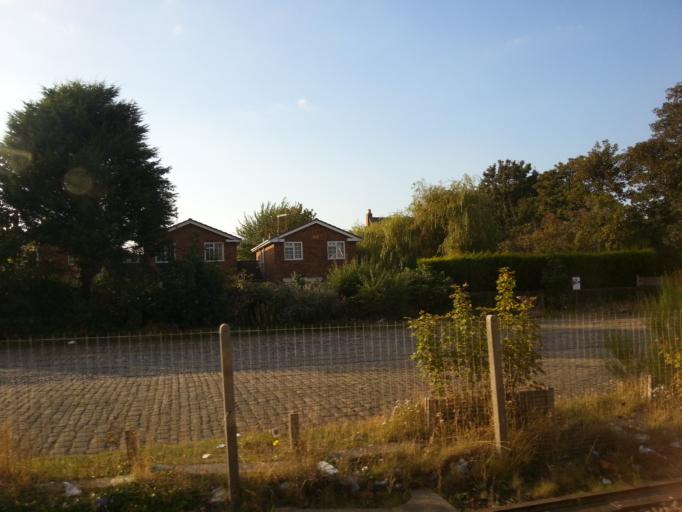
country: GB
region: England
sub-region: Sefton
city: Southport
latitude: 53.6348
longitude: -3.0136
